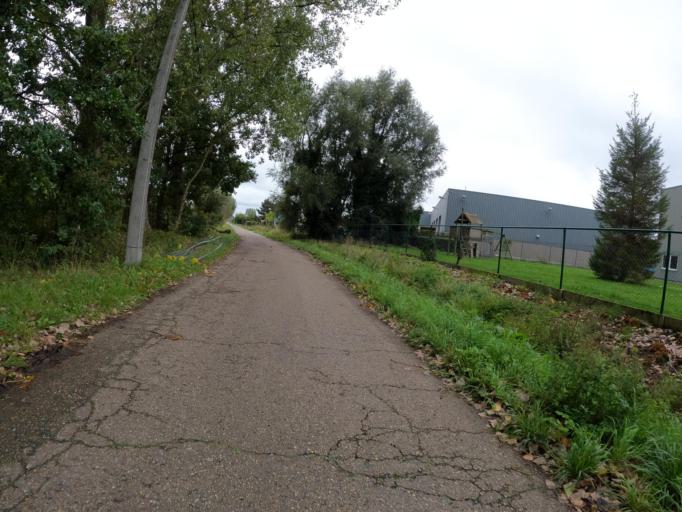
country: BE
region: Flanders
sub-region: Provincie Antwerpen
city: Heist-op-den-Berg
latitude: 51.0624
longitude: 4.7038
